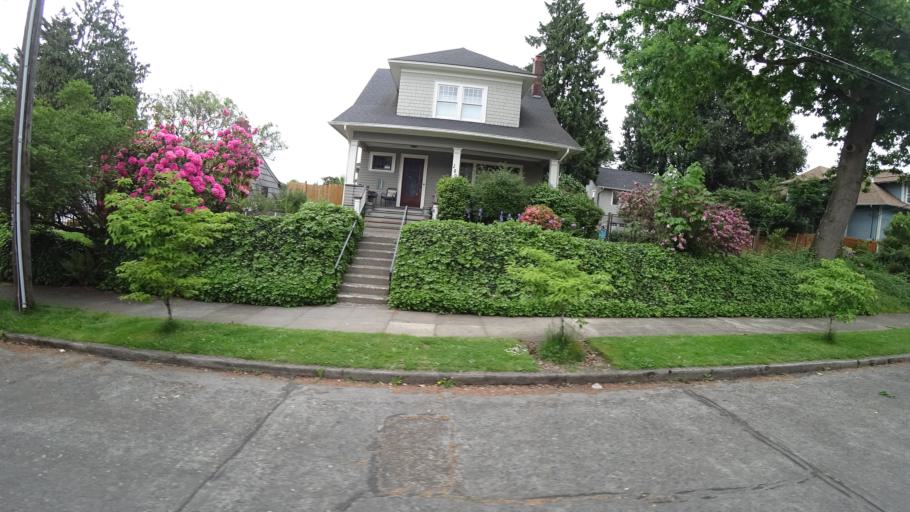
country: US
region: Oregon
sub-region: Multnomah County
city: Lents
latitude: 45.5026
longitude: -122.6140
